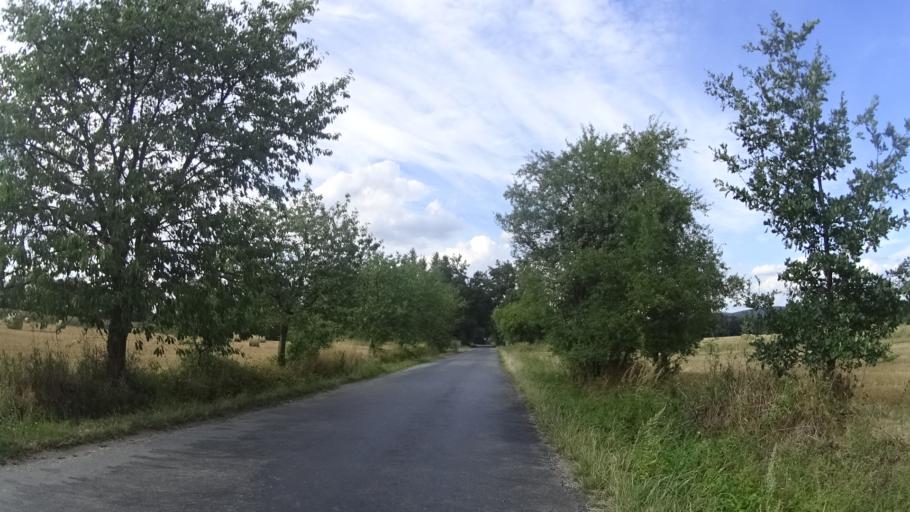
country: CZ
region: Olomoucky
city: Dubicko
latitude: 49.8056
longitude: 16.9417
